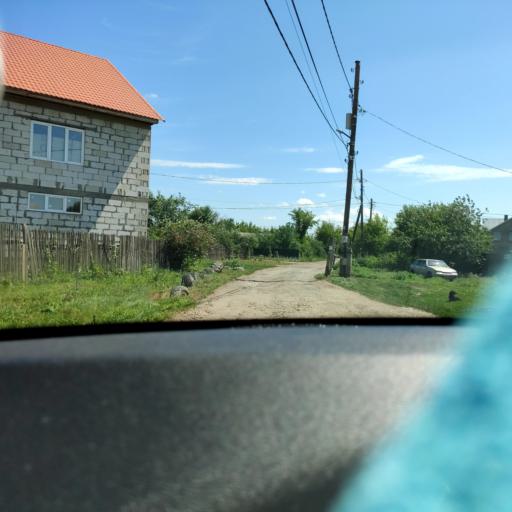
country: RU
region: Samara
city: Smyshlyayevka
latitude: 53.2435
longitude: 50.3525
